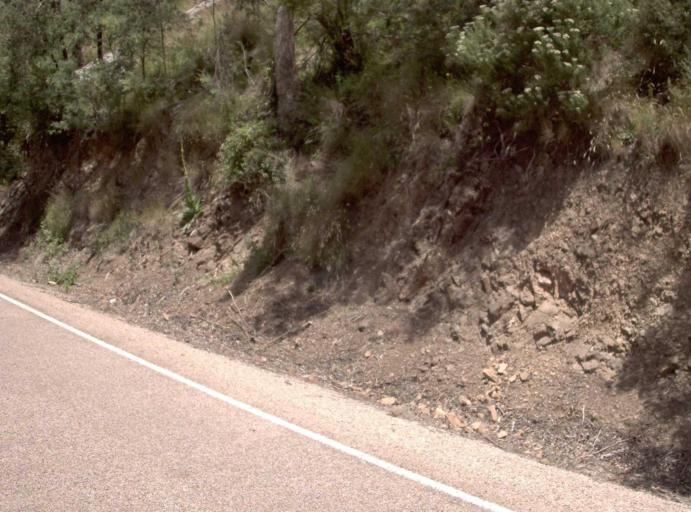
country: AU
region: Victoria
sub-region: East Gippsland
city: Lakes Entrance
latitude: -37.5454
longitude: 147.8661
